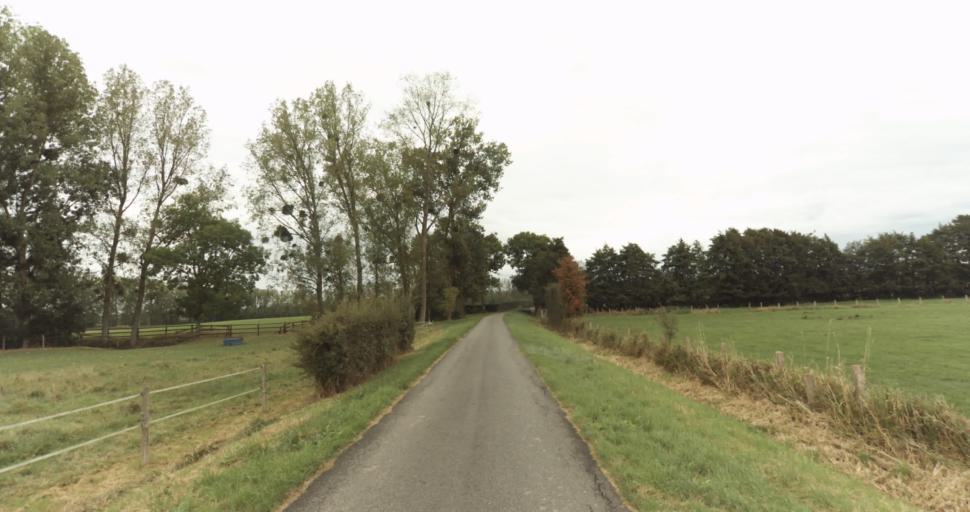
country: FR
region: Lower Normandy
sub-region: Departement de l'Orne
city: Sees
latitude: 48.6652
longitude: 0.2572
